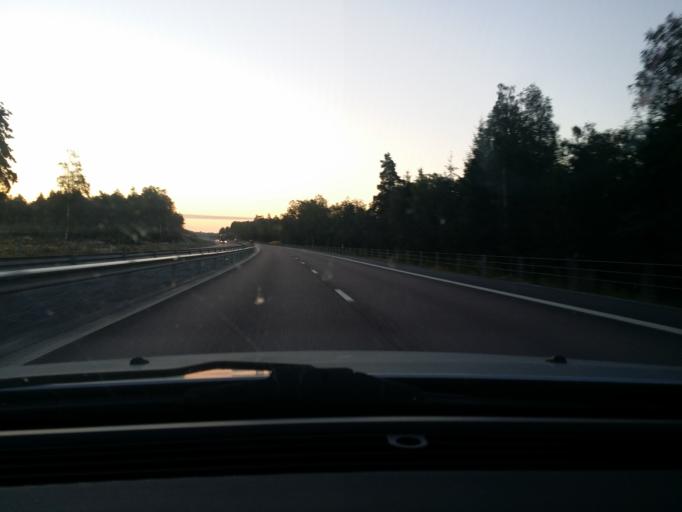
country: SE
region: Vaestmanland
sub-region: Vasteras
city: Tillberga
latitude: 59.6240
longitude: 16.6994
